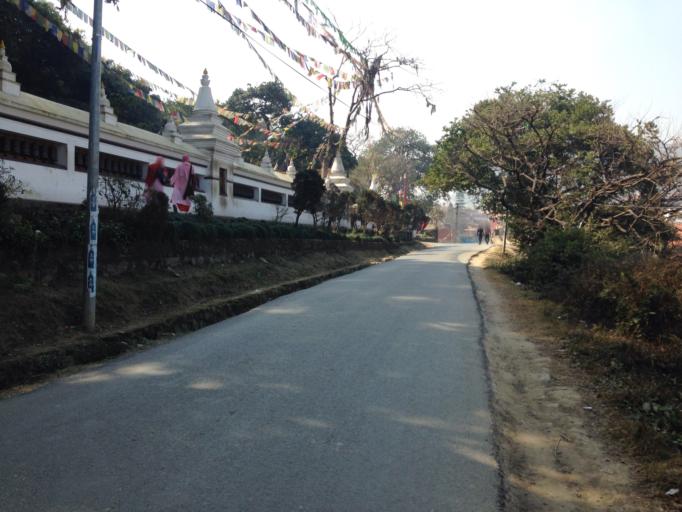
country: NP
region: Central Region
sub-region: Bagmati Zone
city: Kathmandu
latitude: 27.7180
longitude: 85.2886
